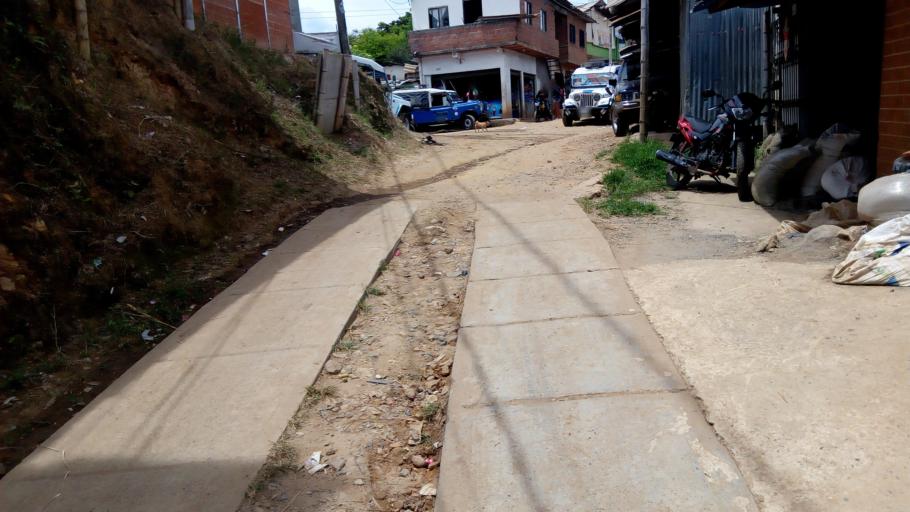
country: CO
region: Valle del Cauca
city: Cali
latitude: 3.3824
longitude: -76.5627
